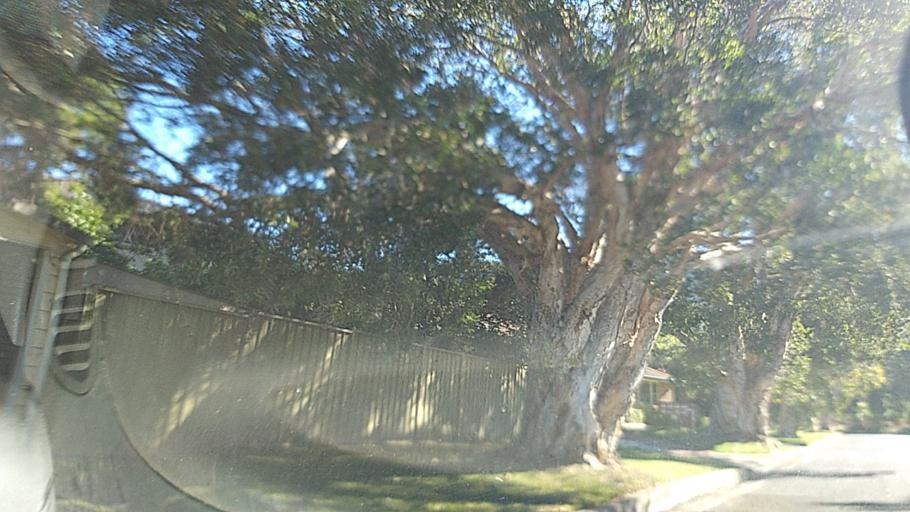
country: AU
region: New South Wales
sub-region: Wollongong
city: Bulli
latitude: -34.3133
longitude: 150.9242
